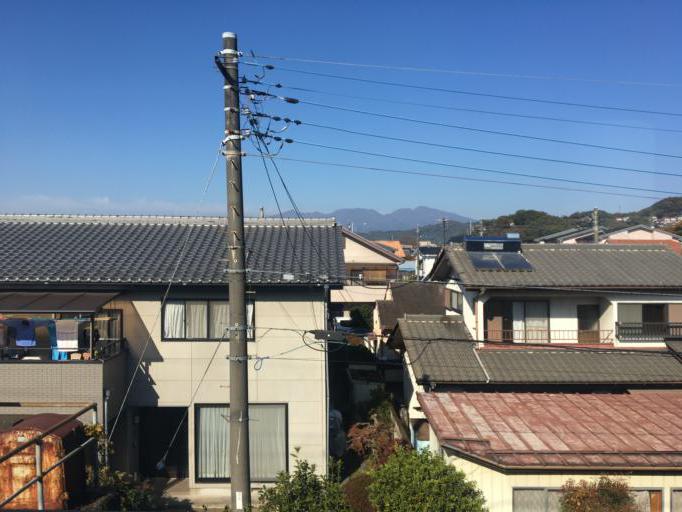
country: JP
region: Gunma
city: Kiryu
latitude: 36.4096
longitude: 139.3182
